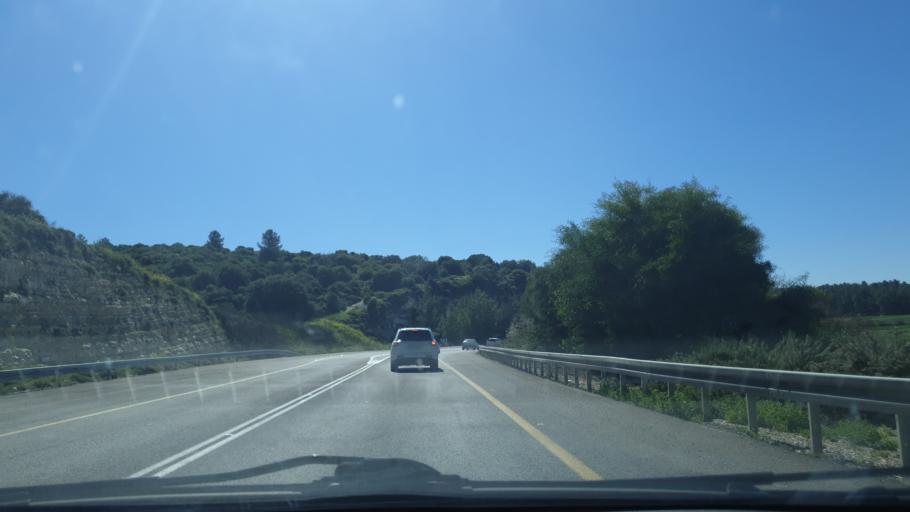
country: IL
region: Jerusalem
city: Bet Shemesh
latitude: 31.6955
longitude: 34.9431
